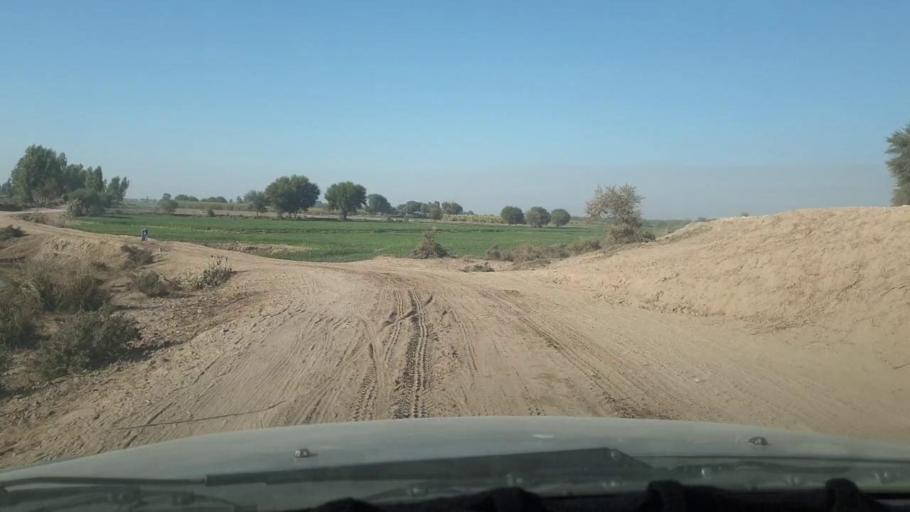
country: PK
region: Sindh
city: Pano Aqil
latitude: 27.9728
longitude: 69.1754
